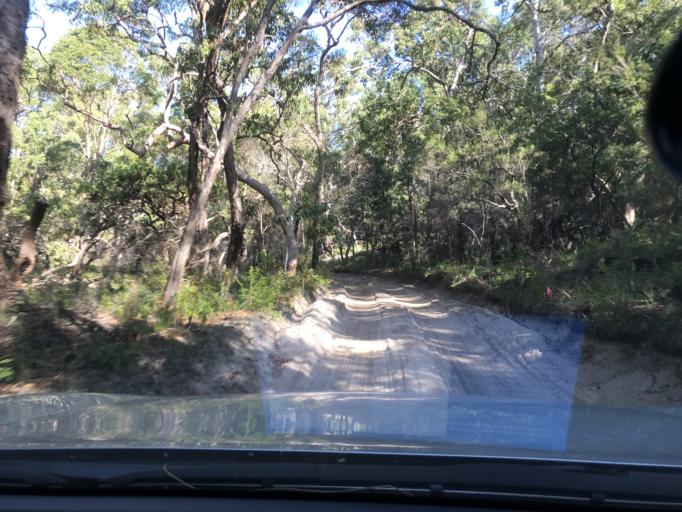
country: AU
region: Queensland
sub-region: Fraser Coast
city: Urangan
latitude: -25.4999
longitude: 153.1047
